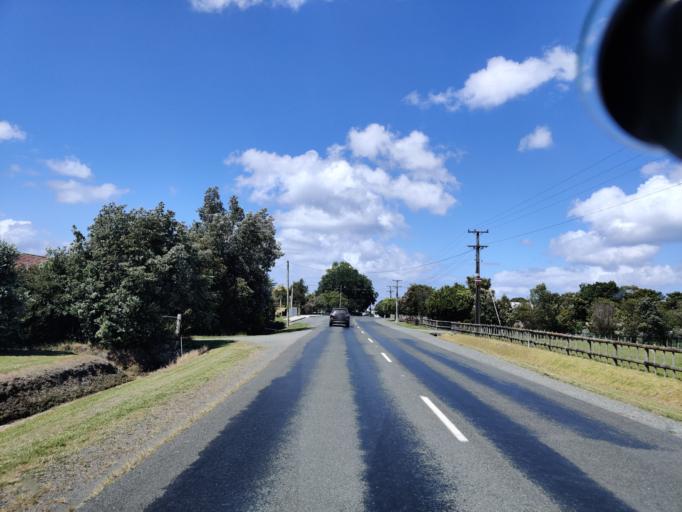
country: NZ
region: Northland
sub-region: Whangarei
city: Ruakaka
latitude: -35.9830
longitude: 174.4365
